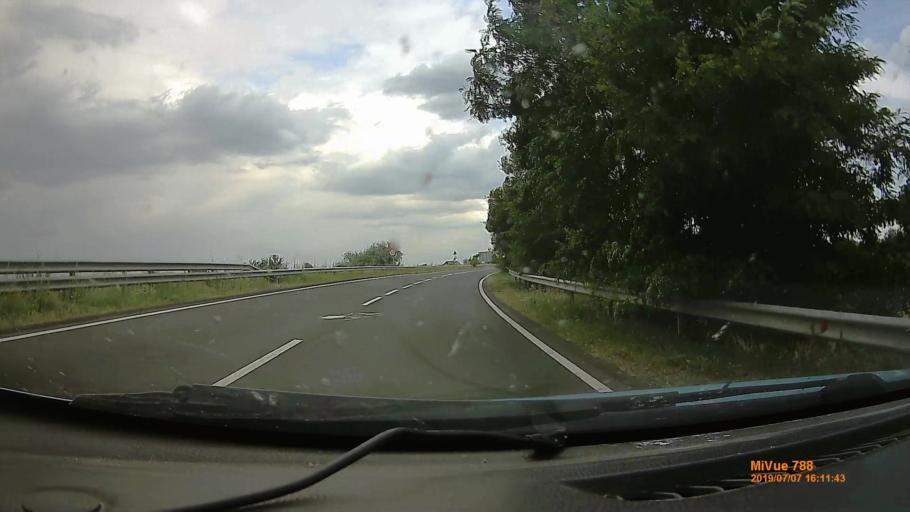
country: HU
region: Heves
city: Hatvan
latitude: 47.6800
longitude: 19.7153
